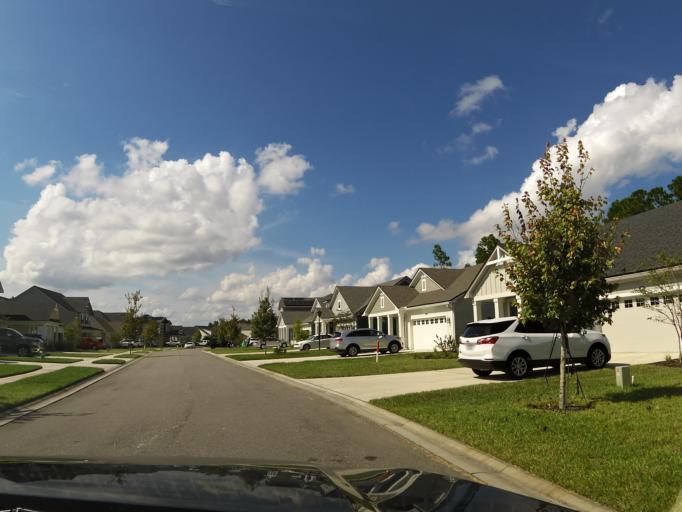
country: US
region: Florida
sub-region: Saint Johns County
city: Palm Valley
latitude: 30.0766
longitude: -81.4657
